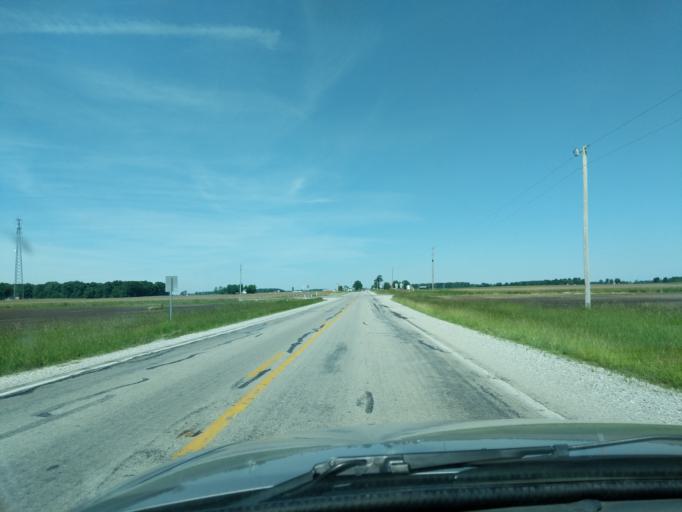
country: US
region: Indiana
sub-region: Huntington County
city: Warren
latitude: 40.6678
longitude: -85.5051
